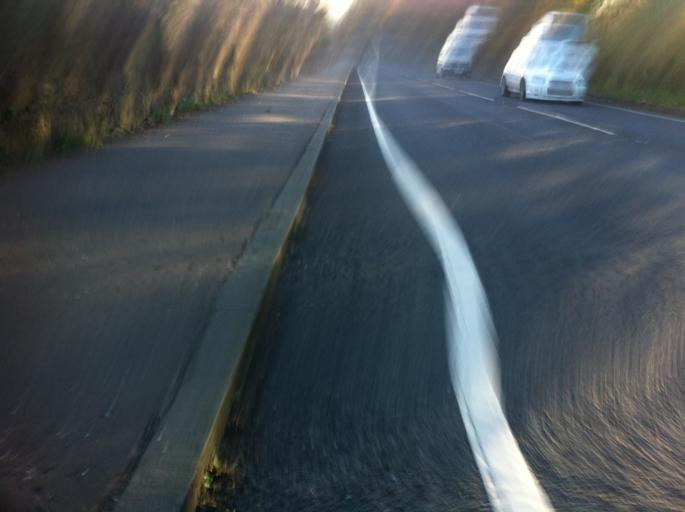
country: GB
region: Scotland
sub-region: East Dunbartonshire
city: Bishopbriggs
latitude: 55.9290
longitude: -4.1954
